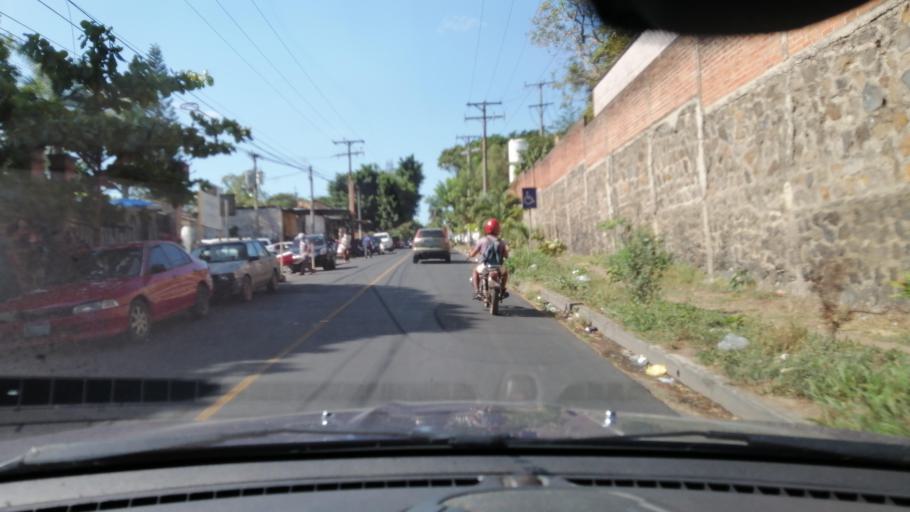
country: SV
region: Santa Ana
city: Santa Ana
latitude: 13.9921
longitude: -89.5504
